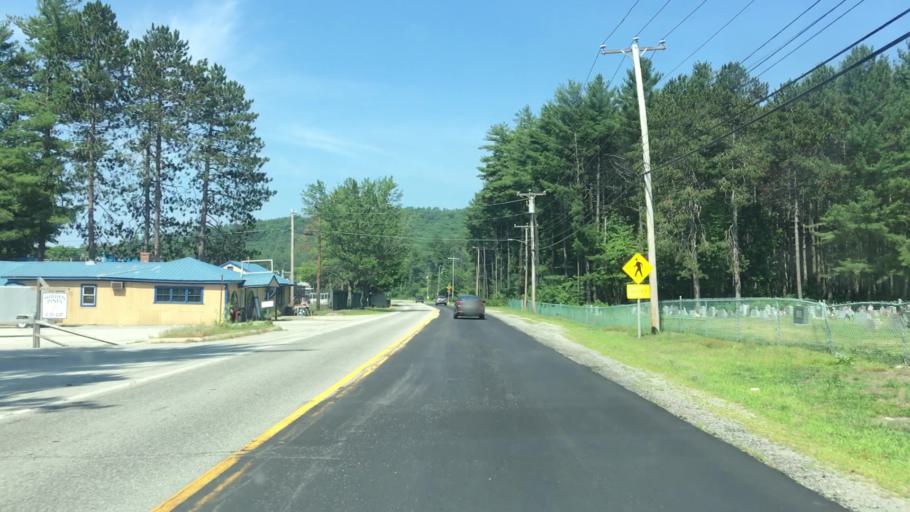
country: US
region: New Hampshire
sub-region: Sullivan County
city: Newport
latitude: 43.3799
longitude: -72.1469
